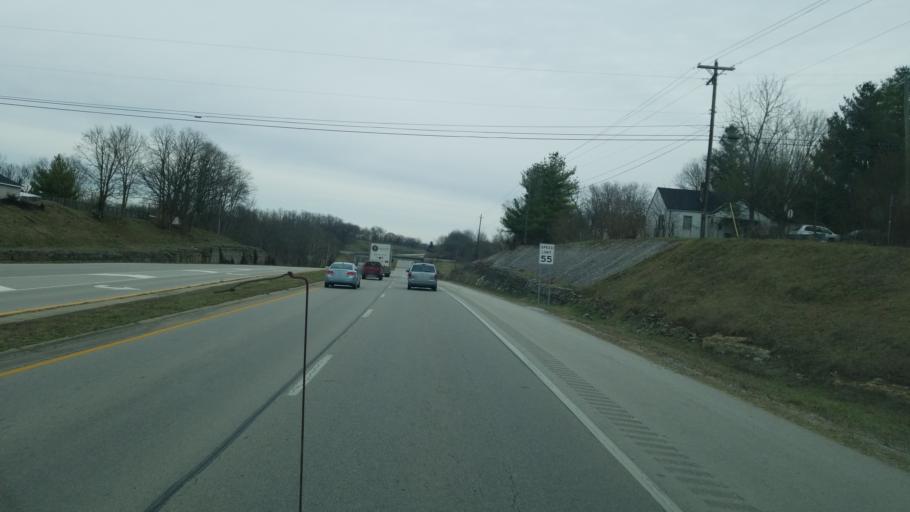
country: US
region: Kentucky
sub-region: Bourbon County
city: Paris
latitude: 38.2255
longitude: -84.2566
